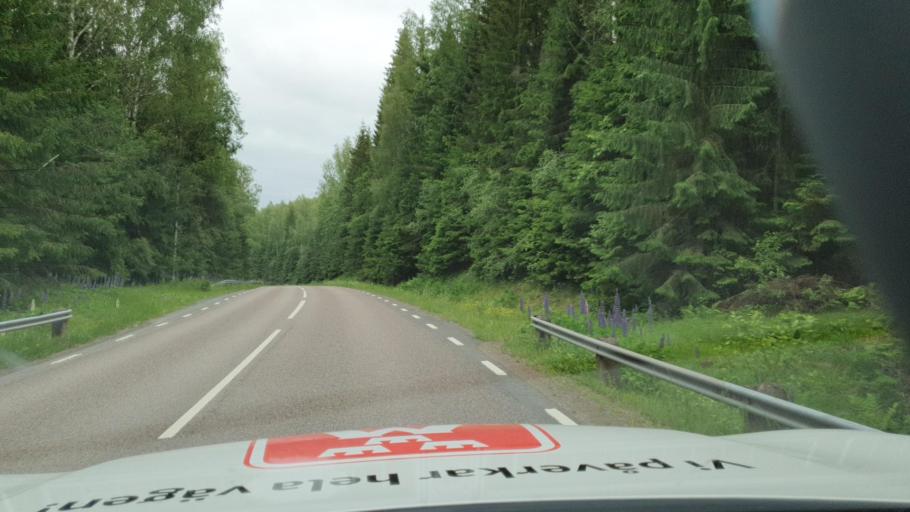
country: SE
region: Vaermland
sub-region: Sunne Kommun
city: Sunne
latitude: 59.8291
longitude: 12.9784
